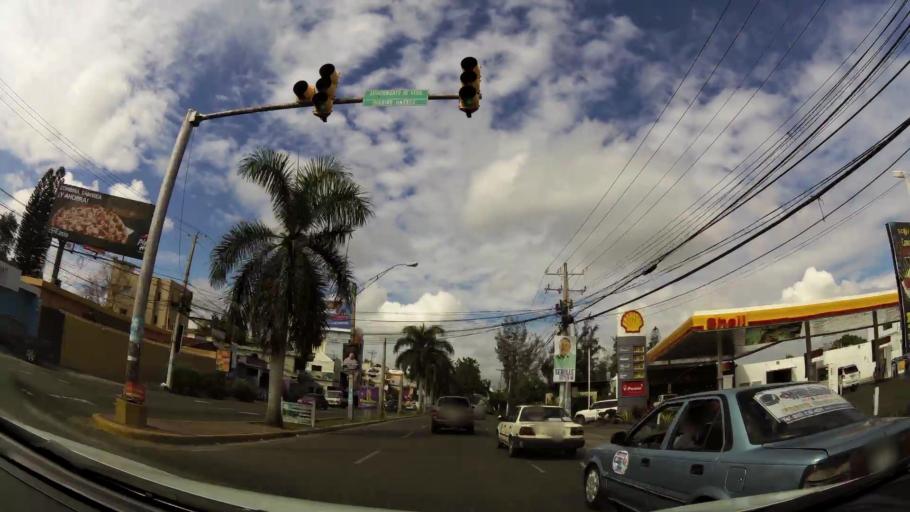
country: DO
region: Santiago
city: Santiago de los Caballeros
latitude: 19.4589
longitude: -70.6940
